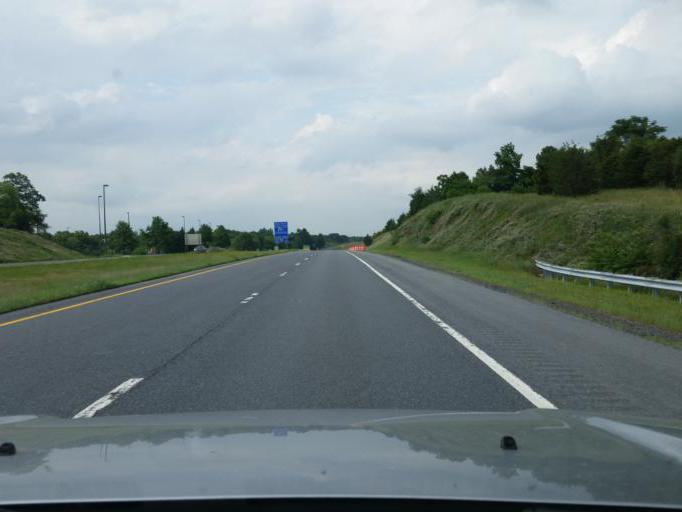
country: US
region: Maryland
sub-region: Frederick County
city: Emmitsburg
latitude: 39.7058
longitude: -77.3130
